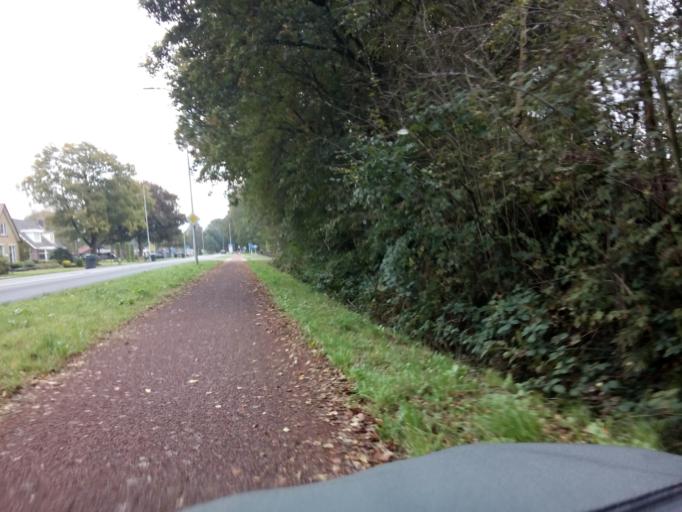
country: NL
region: Gelderland
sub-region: Gemeente Harderwijk
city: Harderwijk
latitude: 52.3579
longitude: 5.6868
